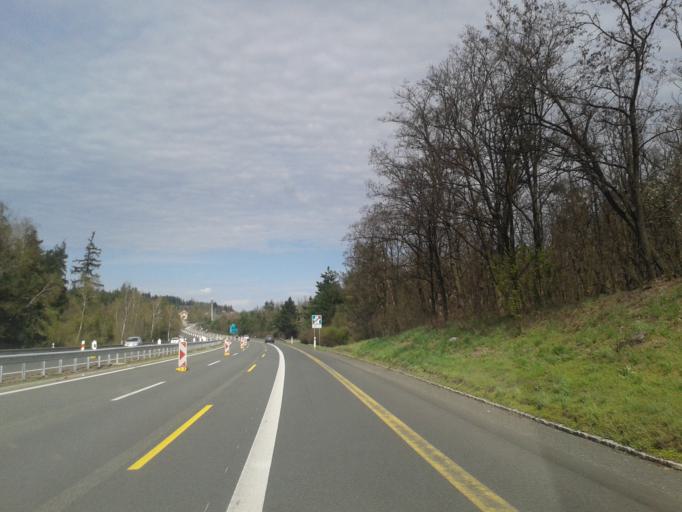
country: CZ
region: Central Bohemia
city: Vsenory
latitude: 49.9152
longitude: 14.3375
